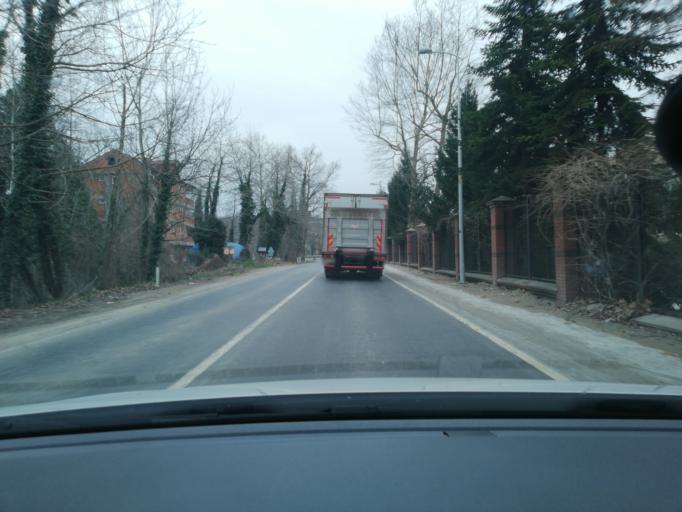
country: TR
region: Zonguldak
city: Gokcebey
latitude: 41.3033
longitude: 32.1248
